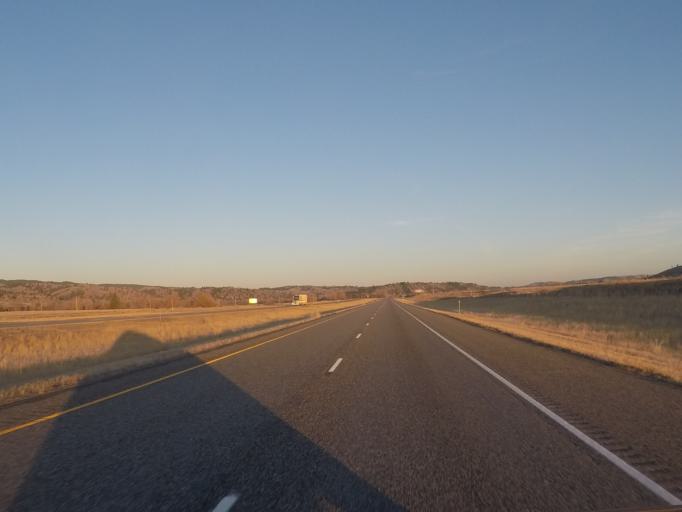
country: US
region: Montana
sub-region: Sweet Grass County
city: Big Timber
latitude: 45.7336
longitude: -109.7003
